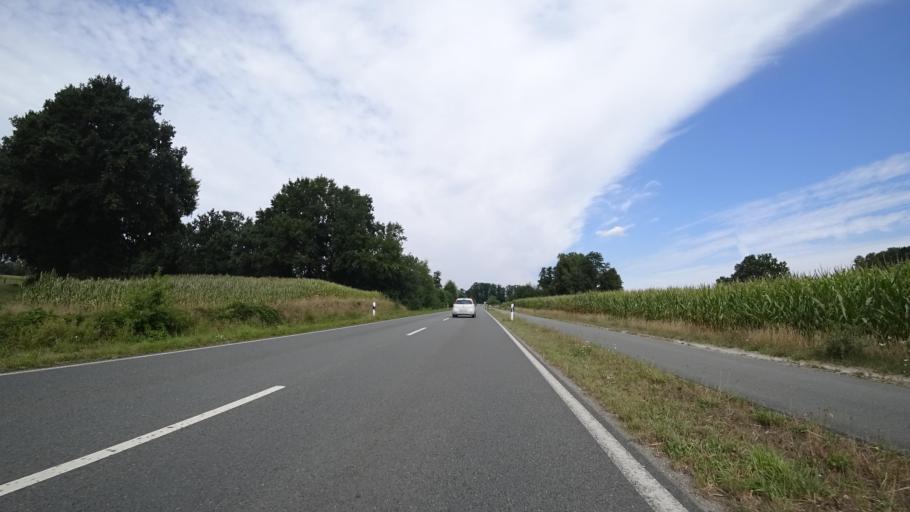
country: DE
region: North Rhine-Westphalia
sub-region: Regierungsbezirk Detmold
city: Guetersloh
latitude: 51.9516
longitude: 8.3806
